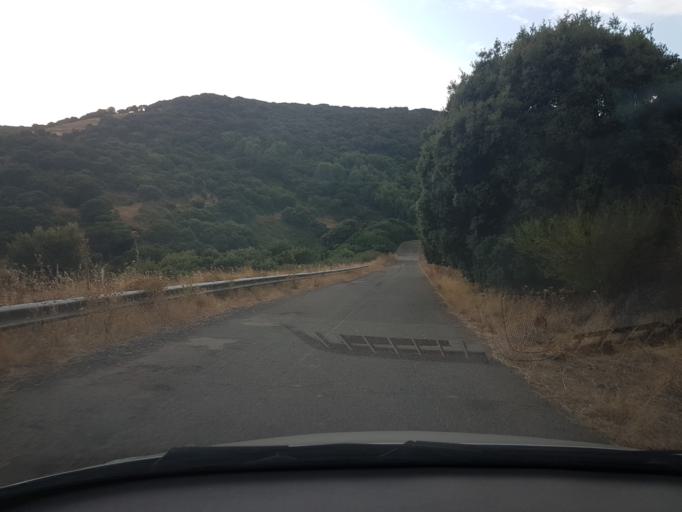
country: IT
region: Sardinia
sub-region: Provincia di Oristano
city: Seneghe
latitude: 40.1111
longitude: 8.6159
